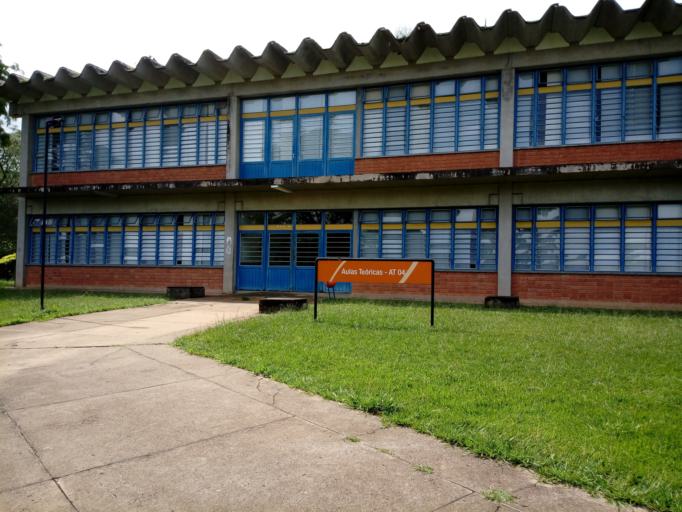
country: BR
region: Sao Paulo
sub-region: Sao Carlos
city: Sao Carlos
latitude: -21.9825
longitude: -47.8840
